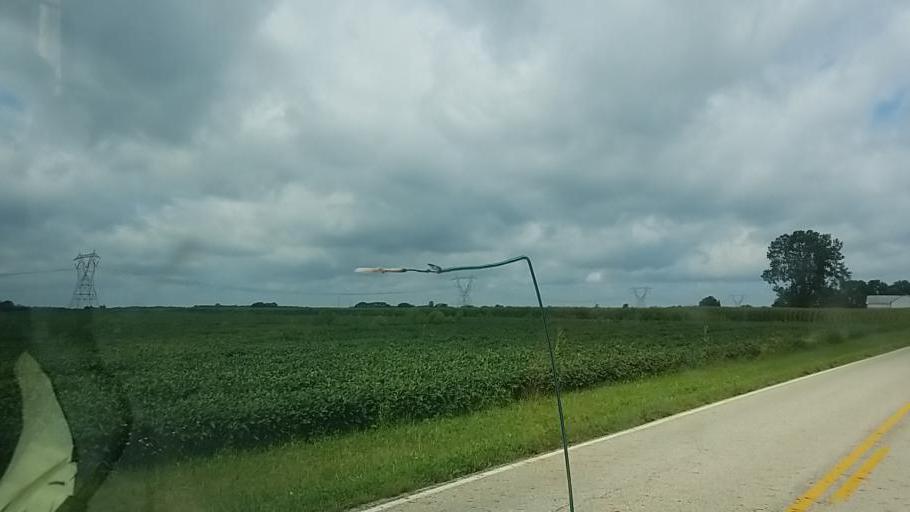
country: US
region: Ohio
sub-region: Madison County
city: Mount Sterling
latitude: 39.7784
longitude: -83.2206
